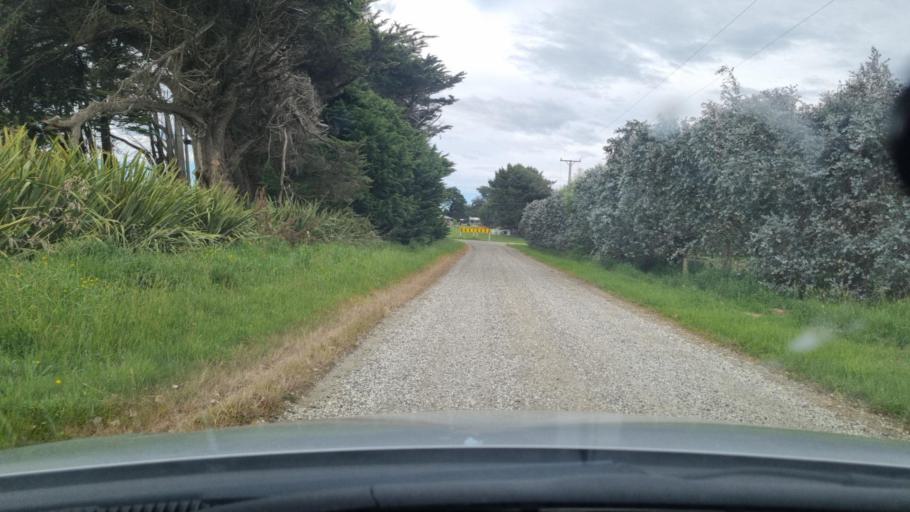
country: NZ
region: Southland
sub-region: Invercargill City
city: Invercargill
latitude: -46.4081
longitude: 168.2598
